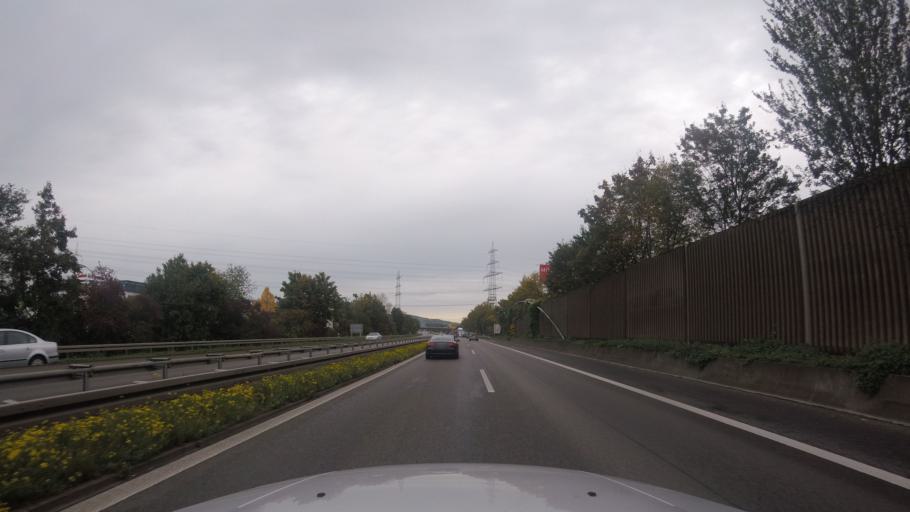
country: DE
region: Baden-Wuerttemberg
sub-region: Regierungsbezirk Stuttgart
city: Weinstadt-Endersbach
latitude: 48.8146
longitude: 9.3739
